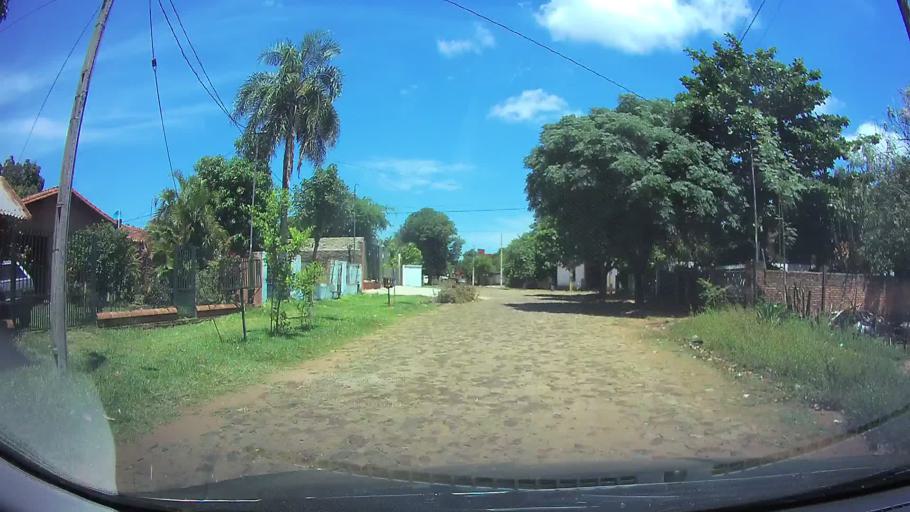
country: PY
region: Central
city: San Lorenzo
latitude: -25.2617
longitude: -57.4867
